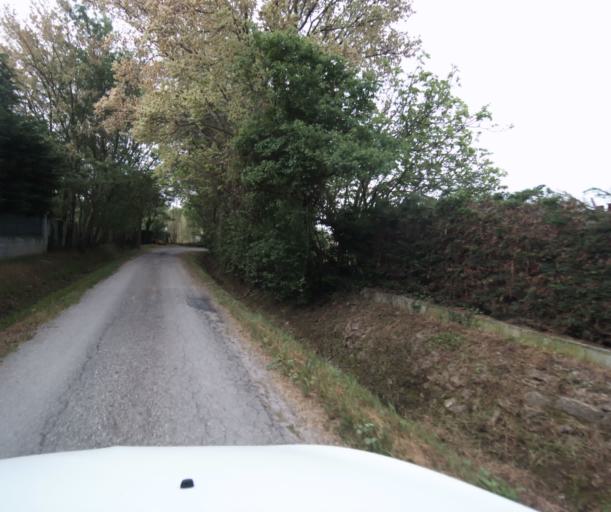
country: FR
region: Provence-Alpes-Cote d'Azur
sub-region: Departement du Var
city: Hyeres
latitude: 43.1114
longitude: 6.1617
